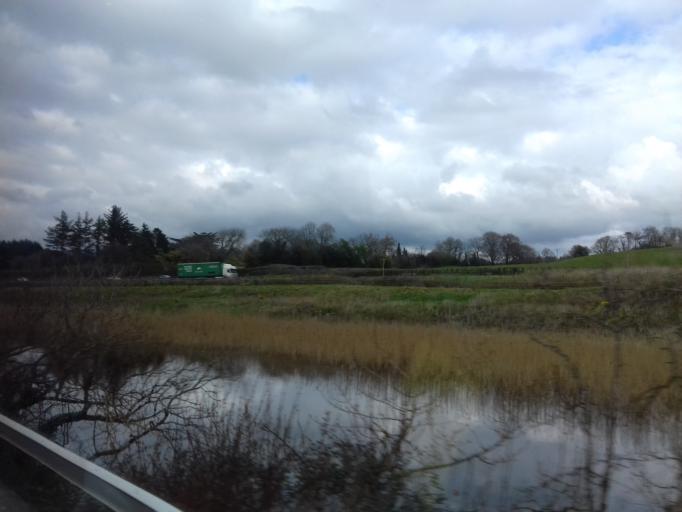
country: IE
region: Leinster
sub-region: An Iarmhi
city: An Muileann gCearr
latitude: 53.5686
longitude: -7.3623
